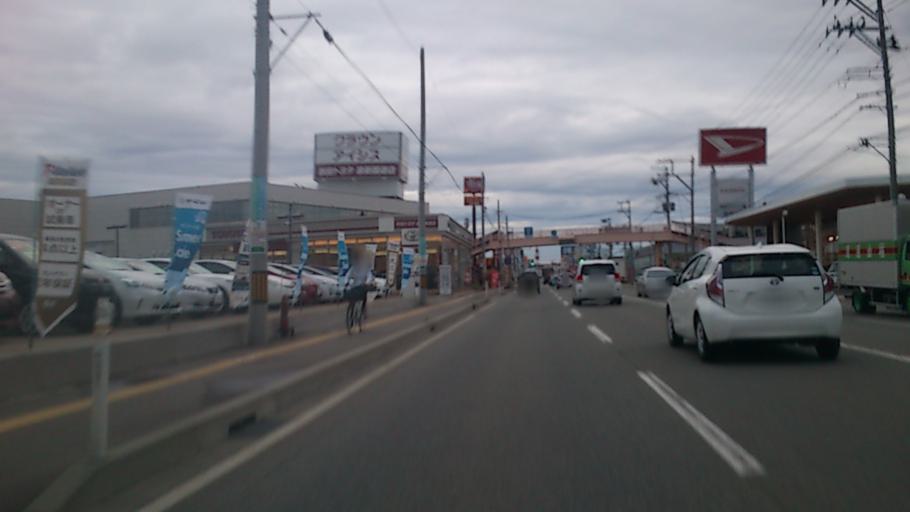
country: JP
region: Akita
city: Akita Shi
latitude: 39.7327
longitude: 140.1015
